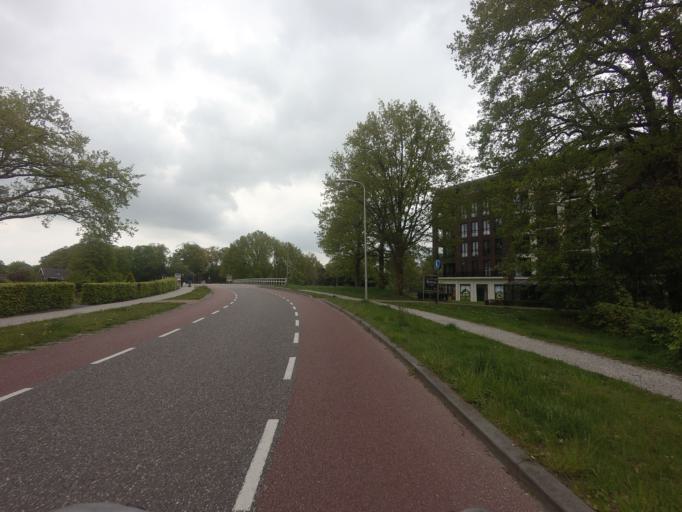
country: NL
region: Overijssel
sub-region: Gemeente Hof van Twente
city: Delden
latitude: 52.2649
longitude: 6.7088
